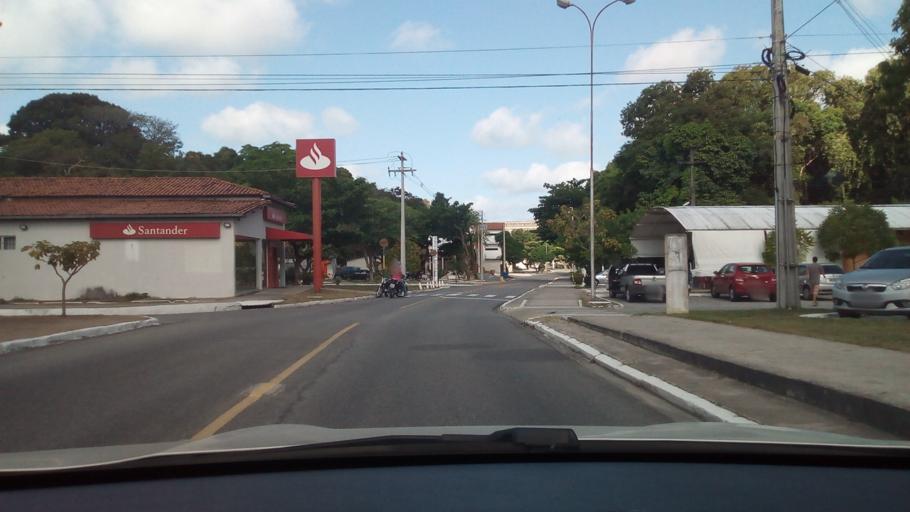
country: BR
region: Paraiba
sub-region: Joao Pessoa
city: Joao Pessoa
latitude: -7.1370
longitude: -34.8451
